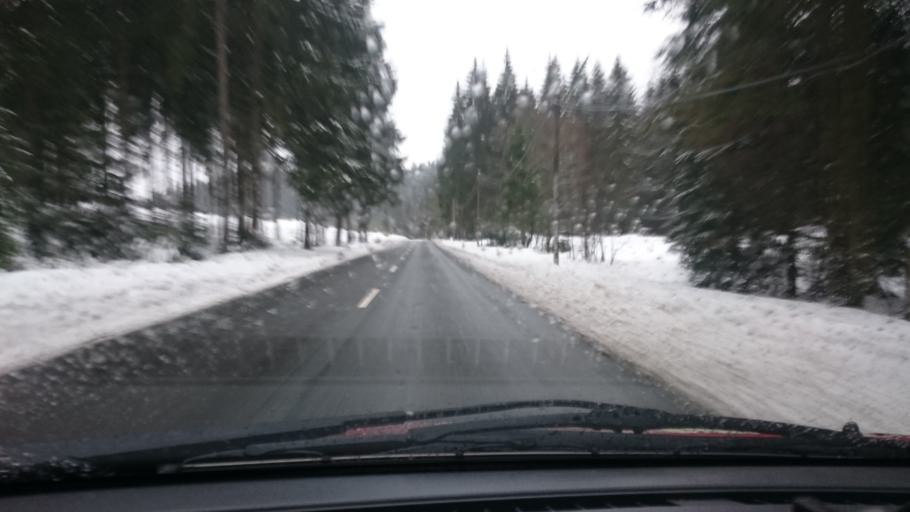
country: DE
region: Saxony
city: Tannenbergsthal
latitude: 50.4145
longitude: 12.4839
